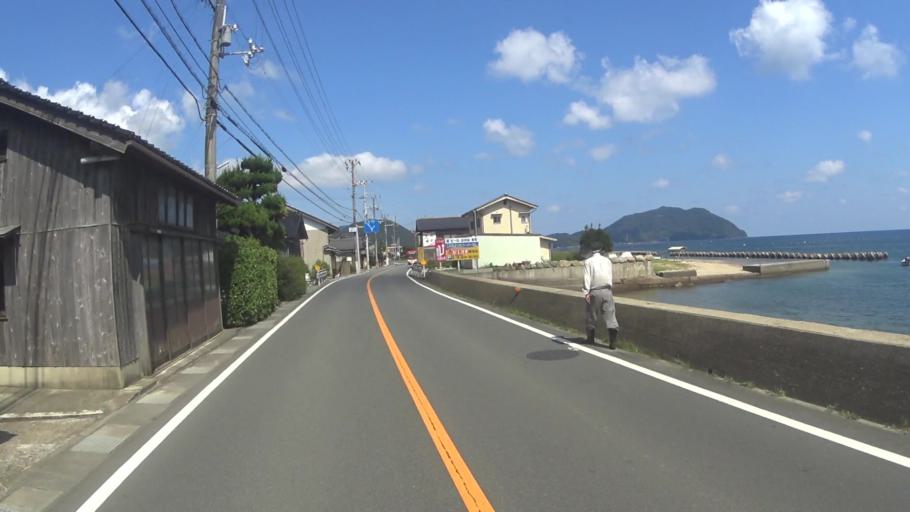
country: JP
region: Kyoto
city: Miyazu
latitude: 35.6547
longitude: 135.2576
